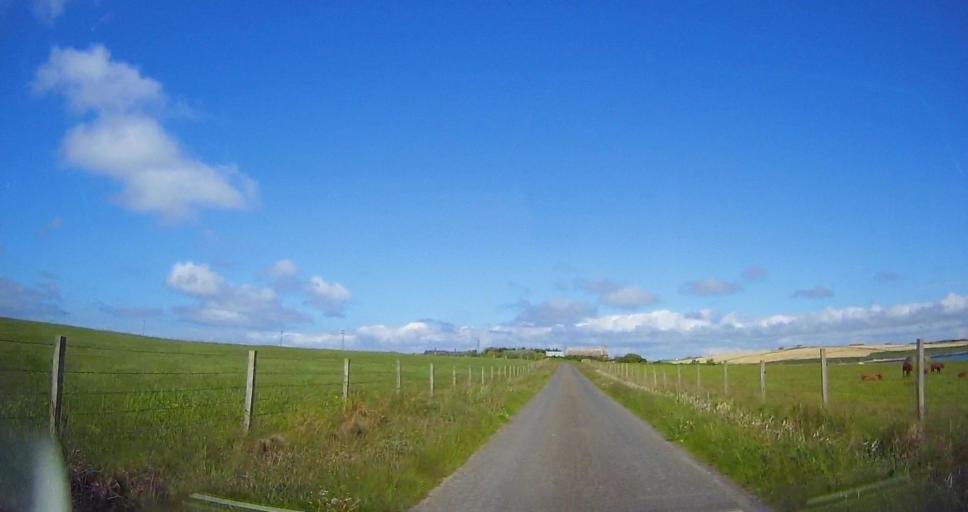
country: GB
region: Scotland
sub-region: Orkney Islands
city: Kirkwall
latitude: 58.8338
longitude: -2.9001
